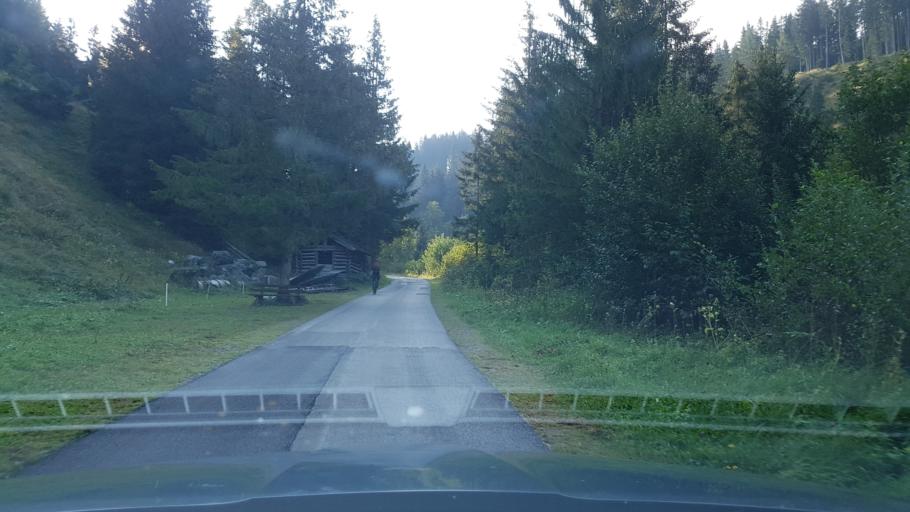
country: AT
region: Salzburg
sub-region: Politischer Bezirk Sankt Johann im Pongau
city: Kleinarl
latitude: 47.2762
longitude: 13.2399
